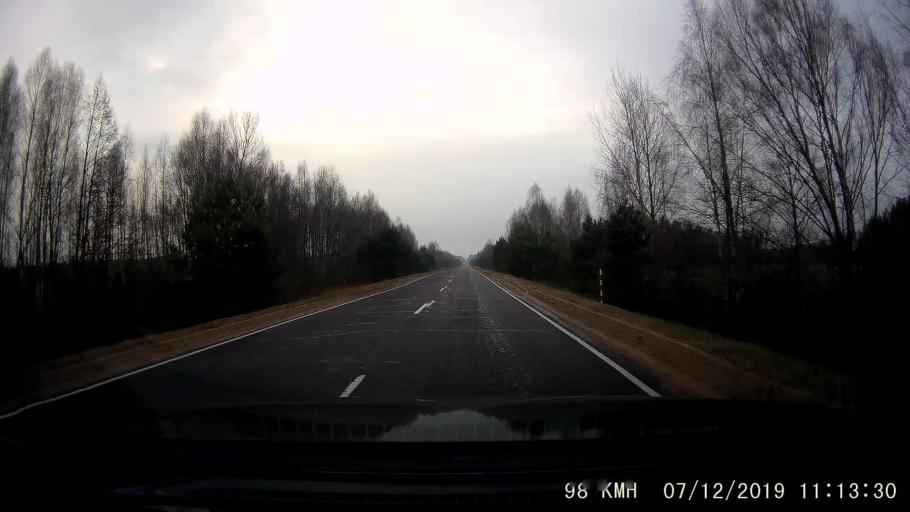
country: BY
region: Grodnenskaya
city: Iwye
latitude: 53.8737
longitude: 25.7399
